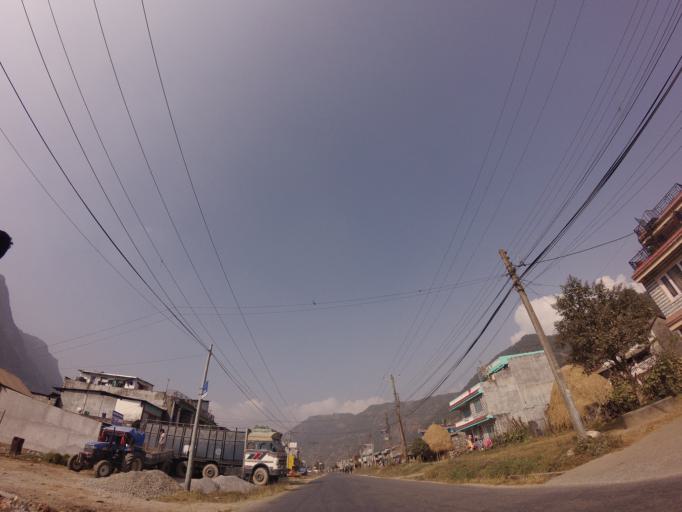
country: NP
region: Western Region
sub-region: Gandaki Zone
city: Pokhara
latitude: 28.2791
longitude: 83.9311
